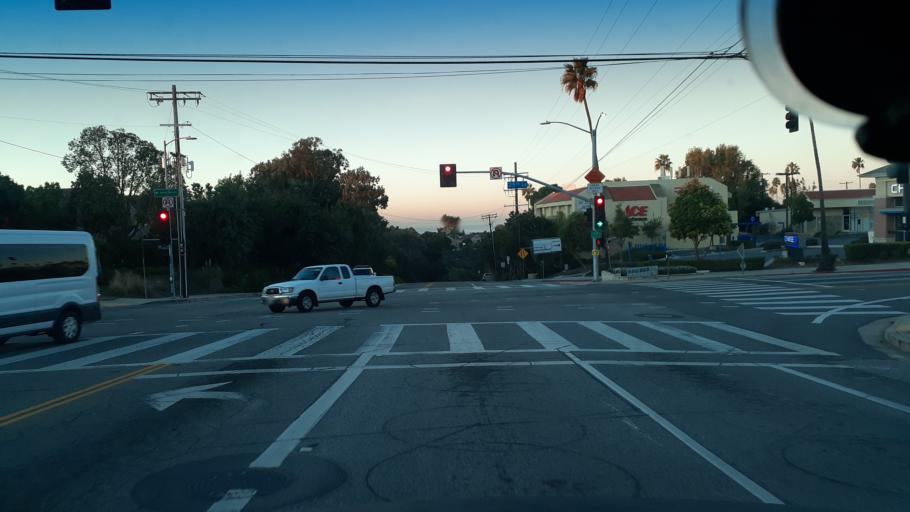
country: US
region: California
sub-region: Los Angeles County
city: San Pedro
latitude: 33.7231
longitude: -118.3128
